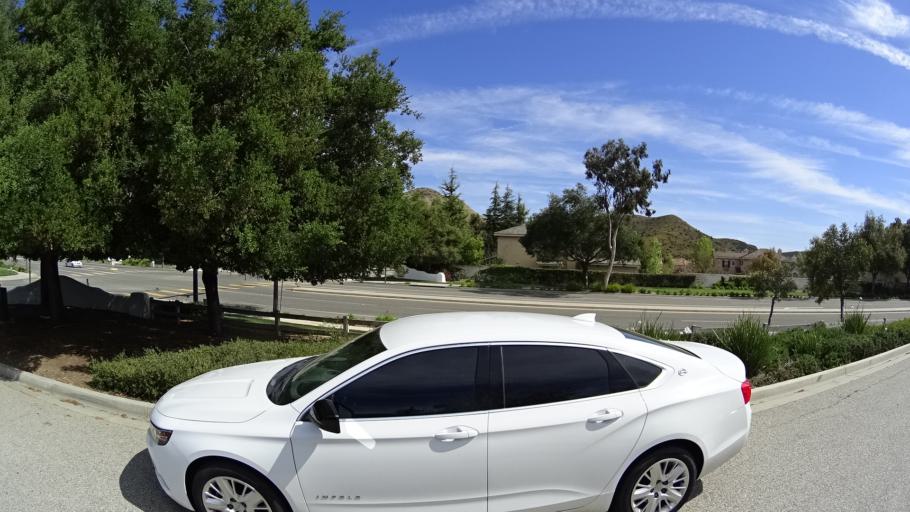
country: US
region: California
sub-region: Ventura County
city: Casa Conejo
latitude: 34.1714
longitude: -118.9765
